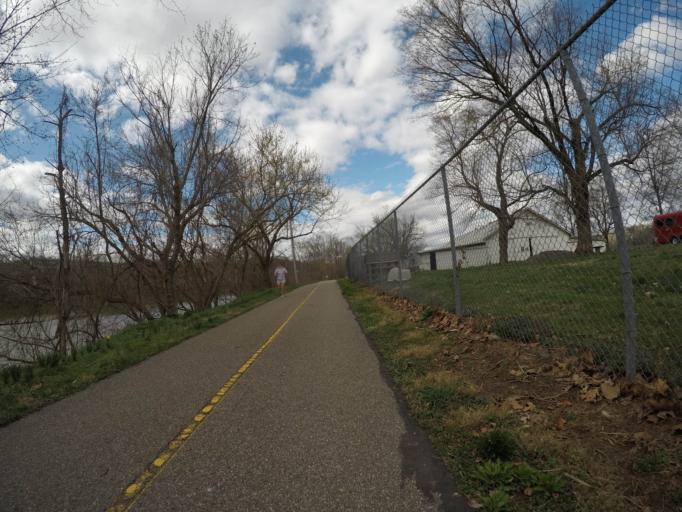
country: US
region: Ohio
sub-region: Washington County
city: Marietta
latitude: 39.4280
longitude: -81.4725
